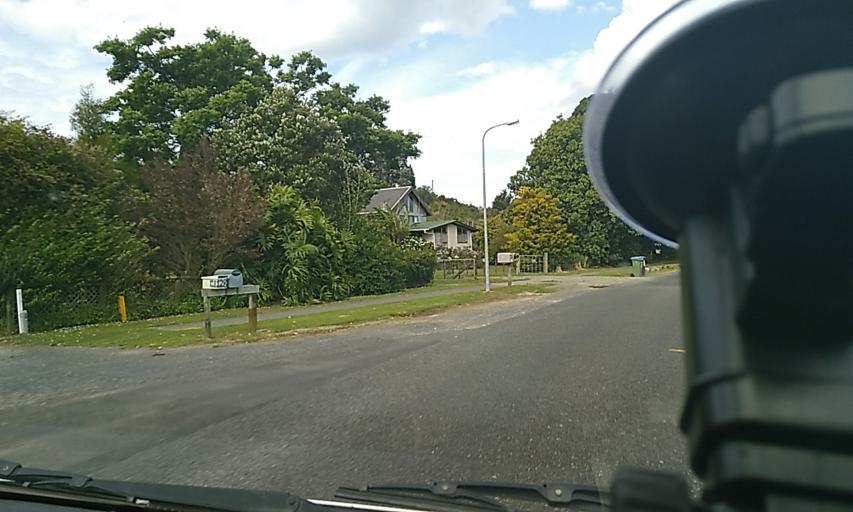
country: NZ
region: Bay of Plenty
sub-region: Western Bay of Plenty District
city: Waihi Beach
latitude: -37.4463
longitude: 175.9581
